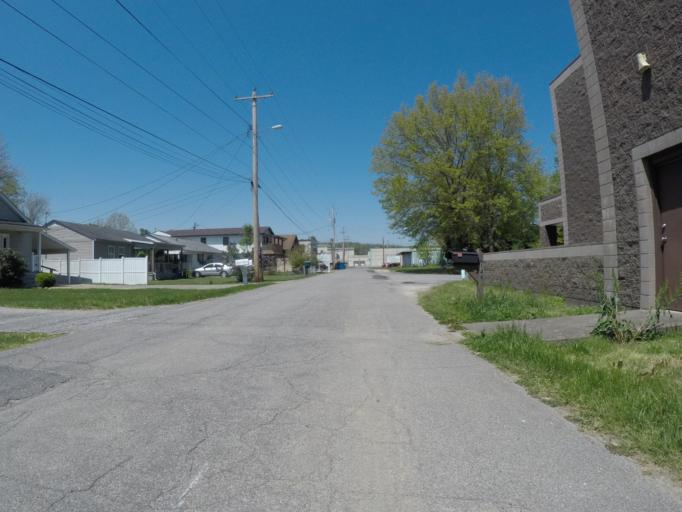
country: US
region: West Virginia
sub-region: Cabell County
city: Barboursville
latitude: 38.4126
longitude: -82.3040
